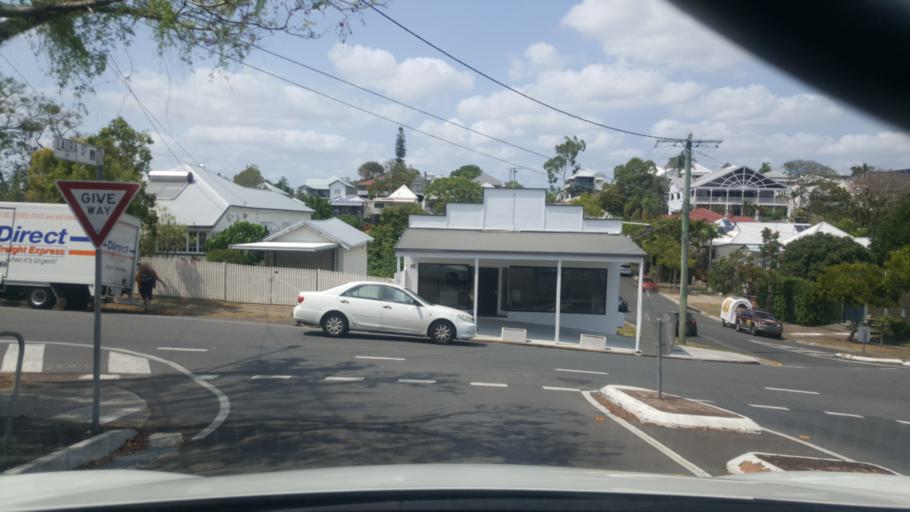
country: AU
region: Queensland
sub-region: Brisbane
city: South Brisbane
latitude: -27.4880
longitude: 153.0223
